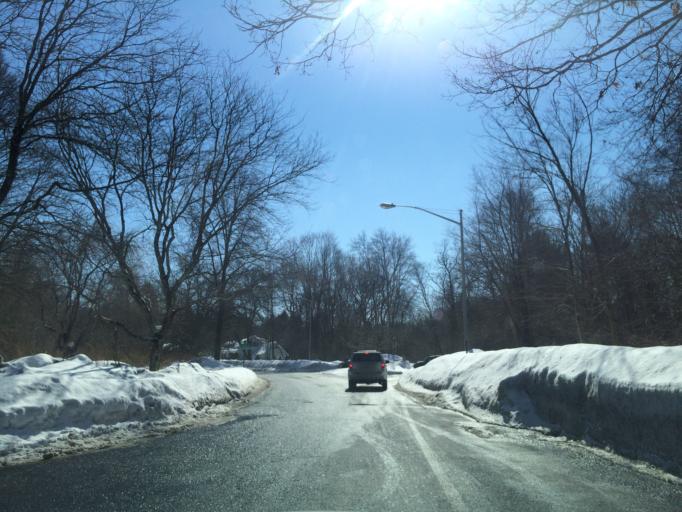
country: US
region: Massachusetts
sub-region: Norfolk County
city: Wellesley
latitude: 42.2953
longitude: -71.2755
